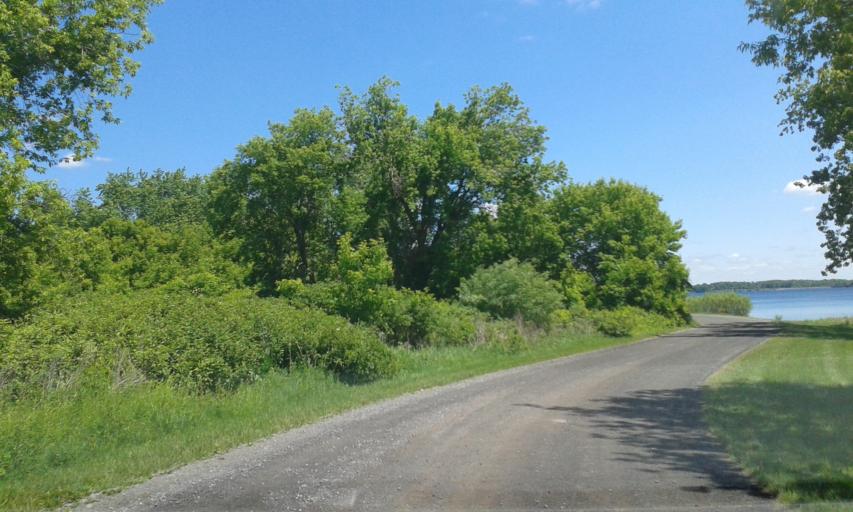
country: US
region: New York
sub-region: St. Lawrence County
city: Massena
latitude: 45.0020
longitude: -74.8933
